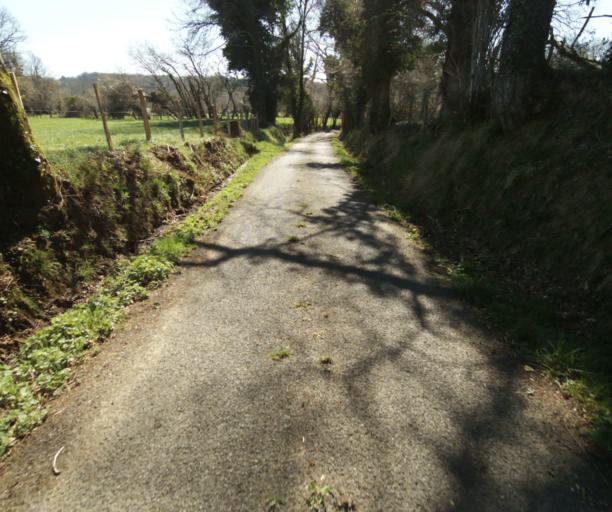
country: FR
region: Limousin
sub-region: Departement de la Correze
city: Chamboulive
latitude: 45.3960
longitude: 1.6677
